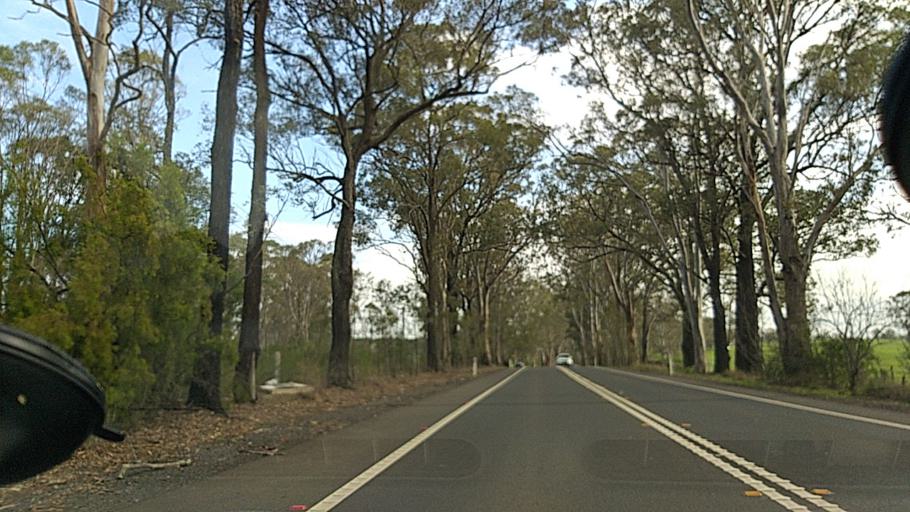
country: AU
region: New South Wales
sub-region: Campbelltown Municipality
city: Glen Alpine
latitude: -34.1190
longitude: 150.7967
